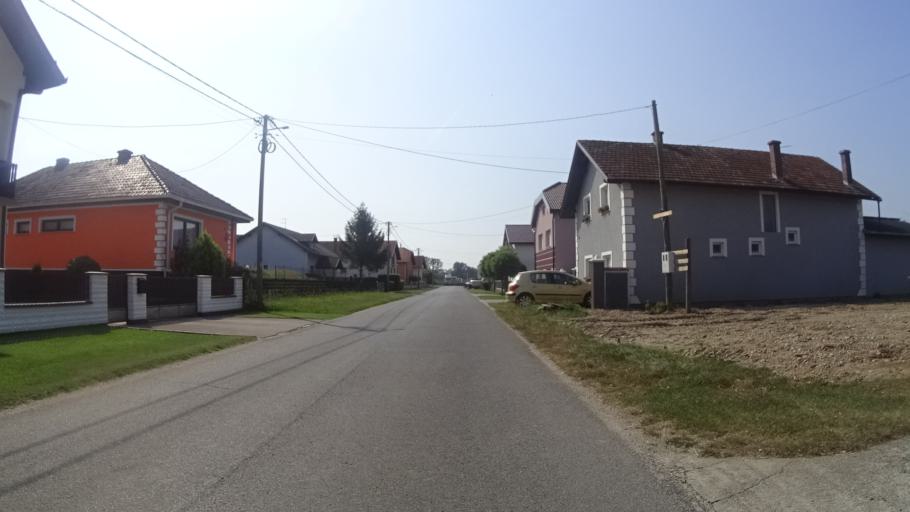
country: HR
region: Medimurska
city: Belica
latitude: 46.3974
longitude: 16.5102
